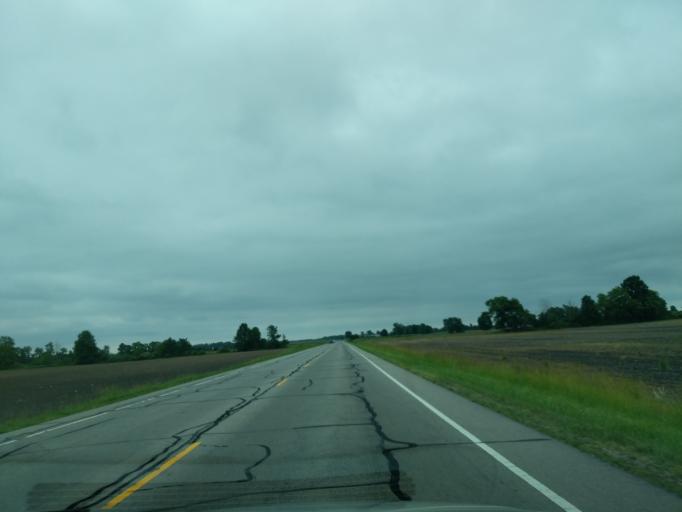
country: US
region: Indiana
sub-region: Madison County
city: Alexandria
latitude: 40.2771
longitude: -85.5840
